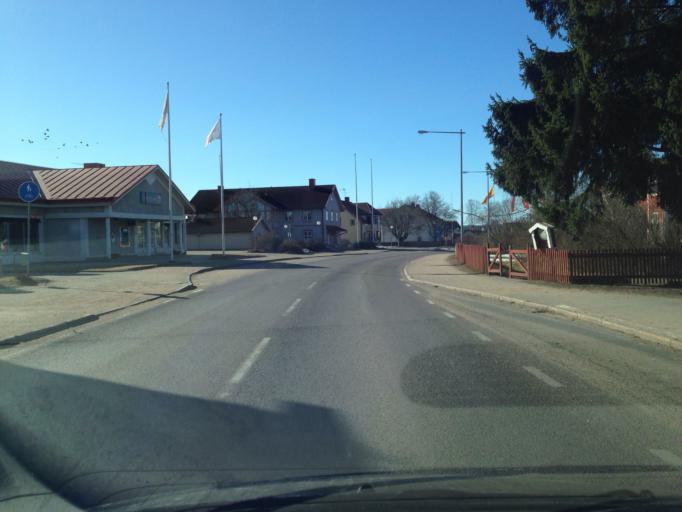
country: SE
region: Gaevleborg
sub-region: Ljusdals Kommun
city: Farila
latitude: 61.7995
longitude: 15.8412
